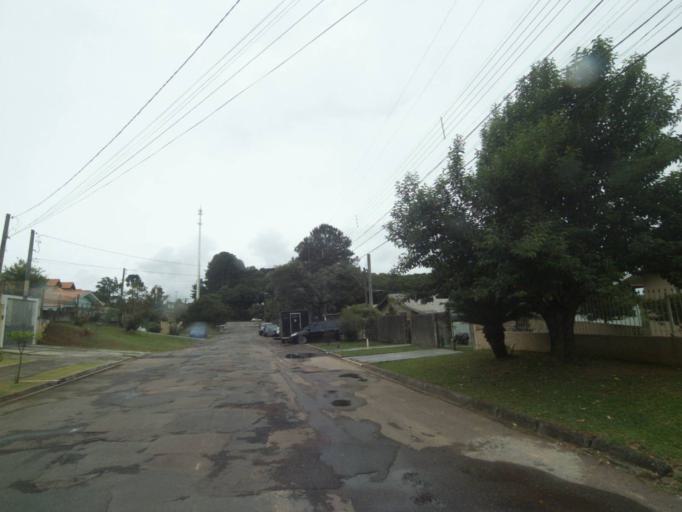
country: BR
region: Parana
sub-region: Curitiba
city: Curitiba
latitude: -25.4287
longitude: -49.3292
